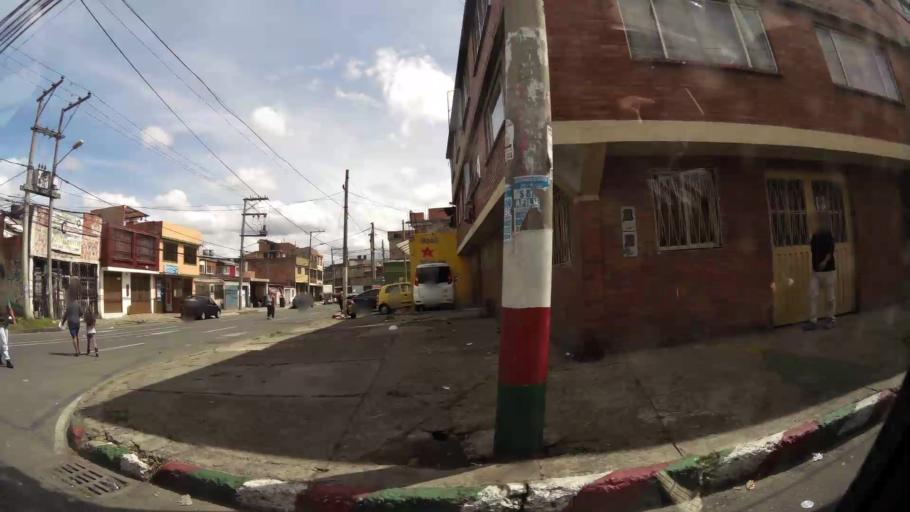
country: CO
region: Bogota D.C.
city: Bogota
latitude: 4.6949
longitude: -74.1159
